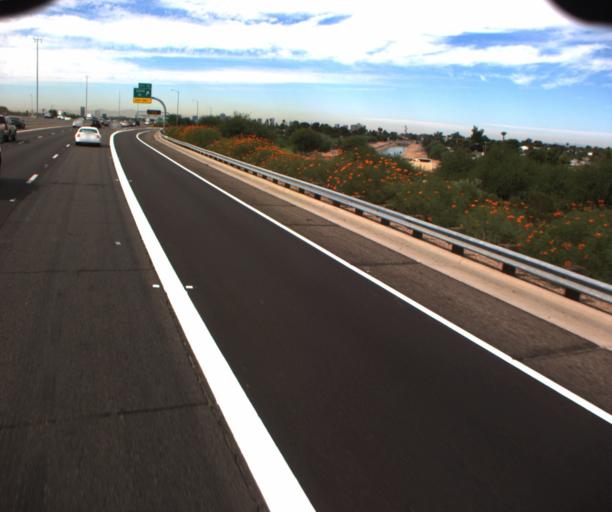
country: US
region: Arizona
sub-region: Maricopa County
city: Phoenix
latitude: 33.4593
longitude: -112.0067
